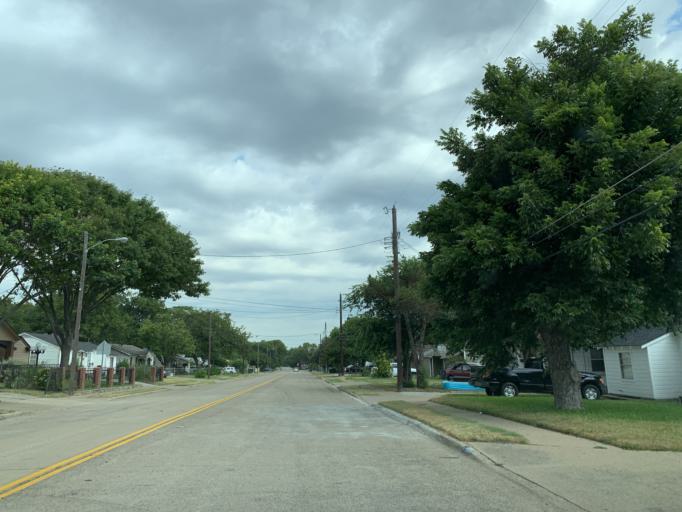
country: US
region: Texas
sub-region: Dallas County
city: Duncanville
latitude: 32.6667
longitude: -96.8290
